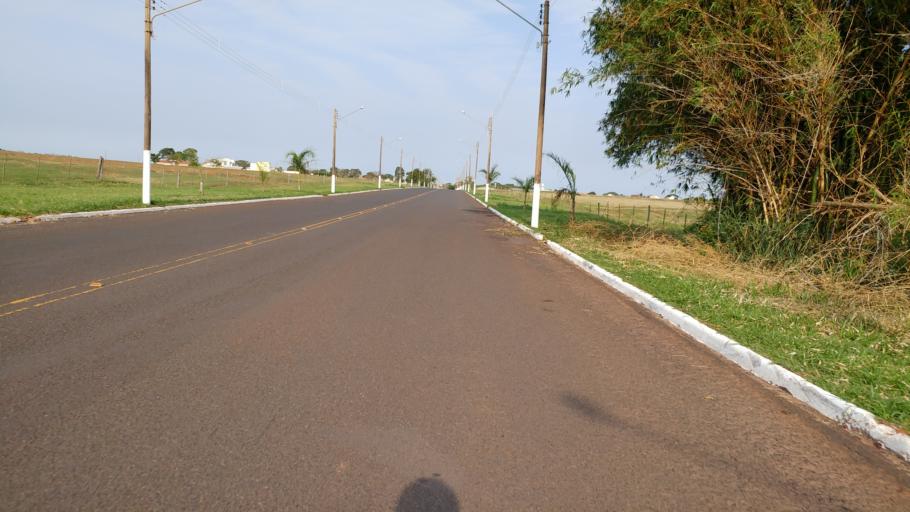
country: BR
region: Sao Paulo
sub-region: Paraguacu Paulista
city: Paraguacu Paulista
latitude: -22.4092
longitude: -50.5964
